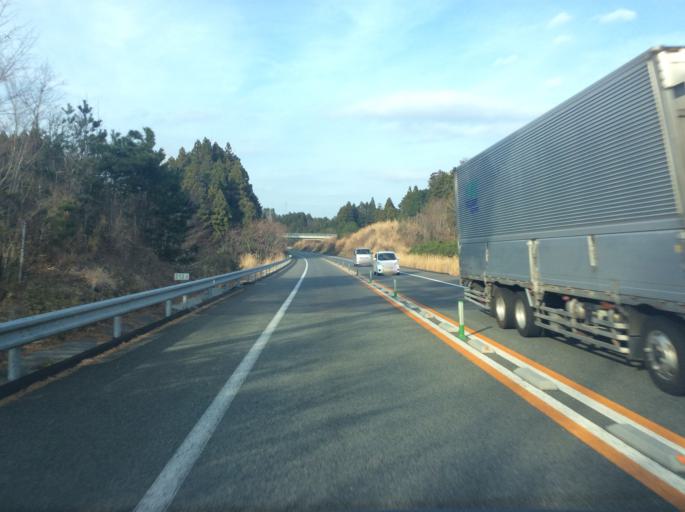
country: JP
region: Fukushima
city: Namie
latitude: 37.3359
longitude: 140.9906
